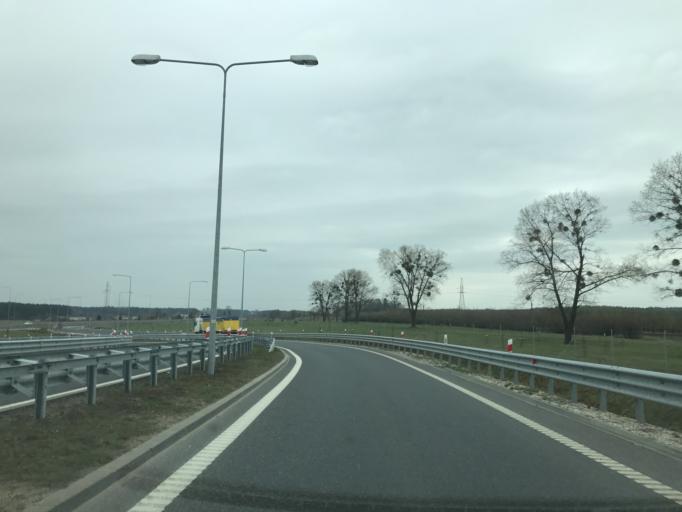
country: PL
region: Warmian-Masurian Voivodeship
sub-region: Powiat olsztynski
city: Olsztynek
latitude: 53.6029
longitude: 20.3065
